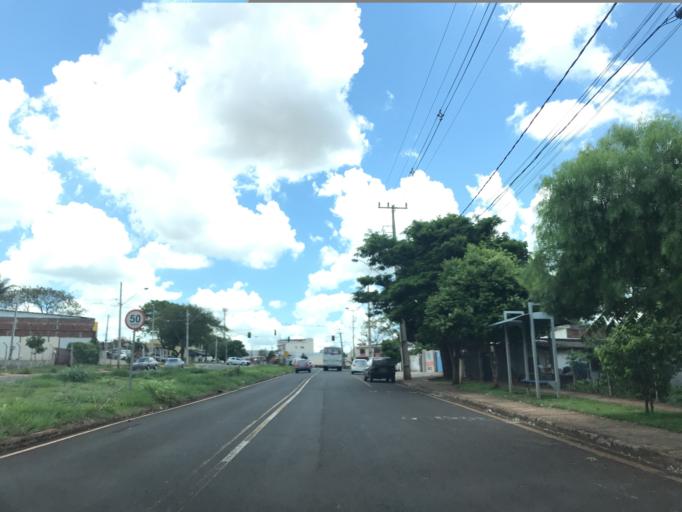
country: BR
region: Parana
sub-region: Maringa
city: Maringa
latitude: -23.3892
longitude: -51.9150
